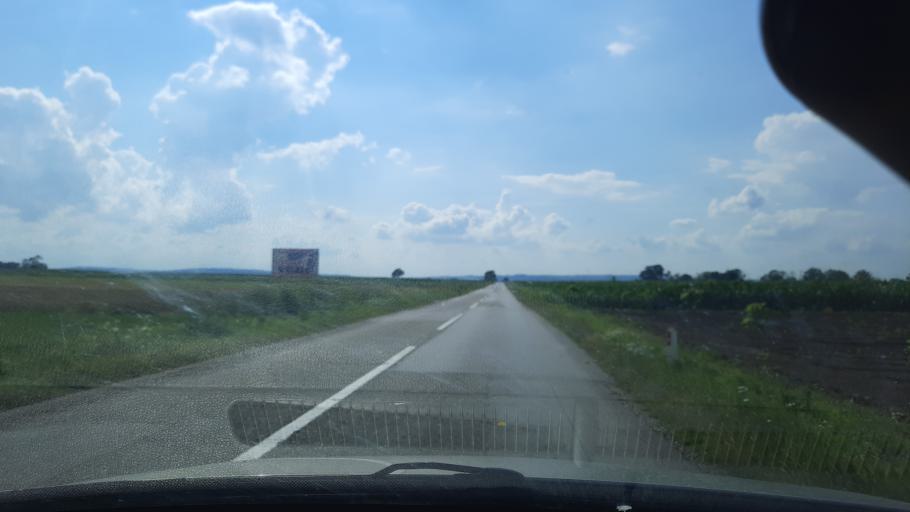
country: RS
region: Central Serbia
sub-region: Branicevski Okrug
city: Malo Crnice
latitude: 44.5811
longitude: 21.3153
